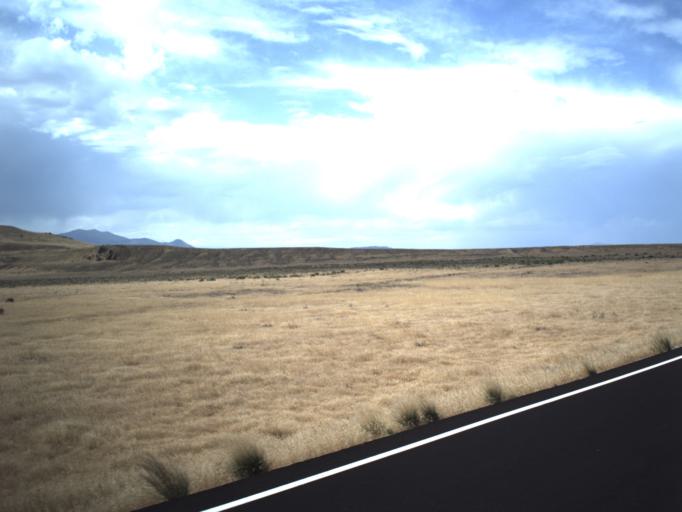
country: US
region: Utah
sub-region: Tooele County
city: Wendover
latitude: 41.4206
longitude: -113.8978
